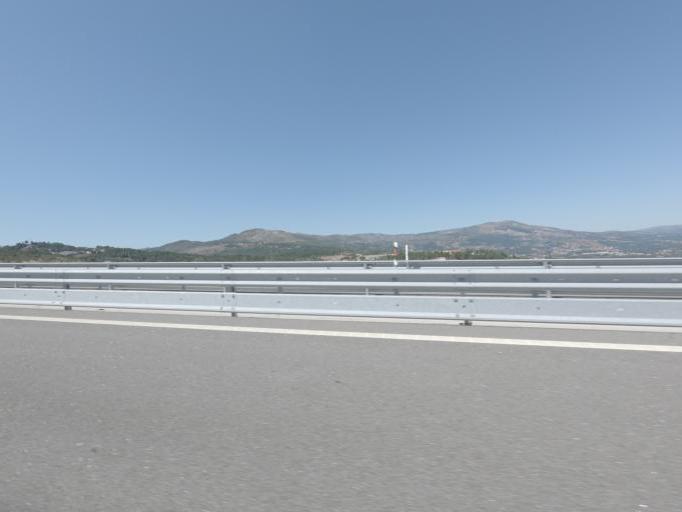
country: PT
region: Vila Real
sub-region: Santa Marta de Penaguiao
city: Santa Marta de Penaguiao
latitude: 41.2646
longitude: -7.7970
